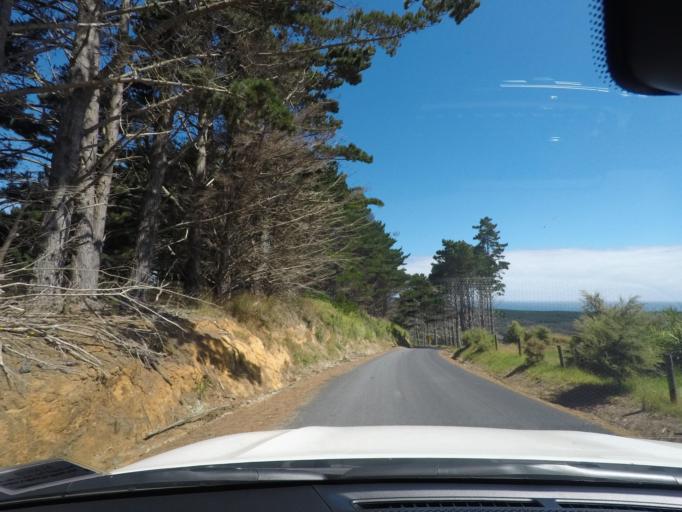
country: NZ
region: Auckland
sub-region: Auckland
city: Parakai
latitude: -36.5871
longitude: 174.2871
